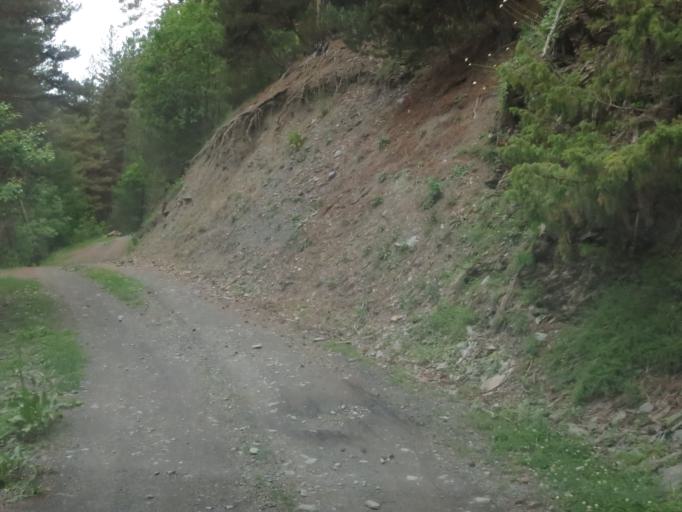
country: RU
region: Chechnya
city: Itum-Kali
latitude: 42.3641
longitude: 45.6537
